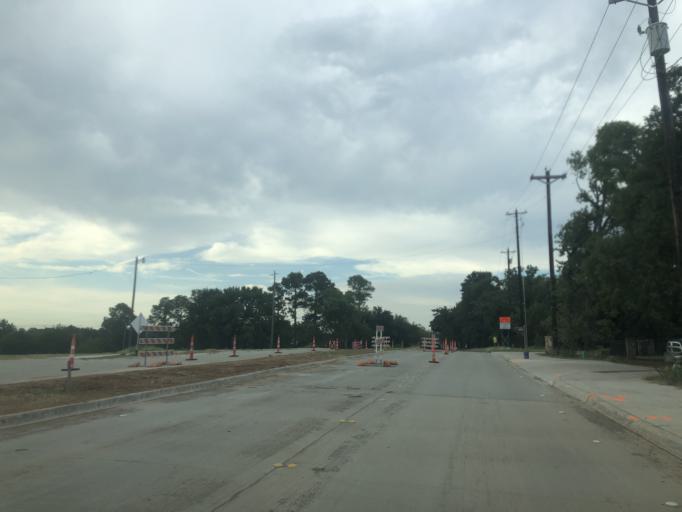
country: US
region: Texas
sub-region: Tarrant County
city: Southlake
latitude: 32.9555
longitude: -97.1512
